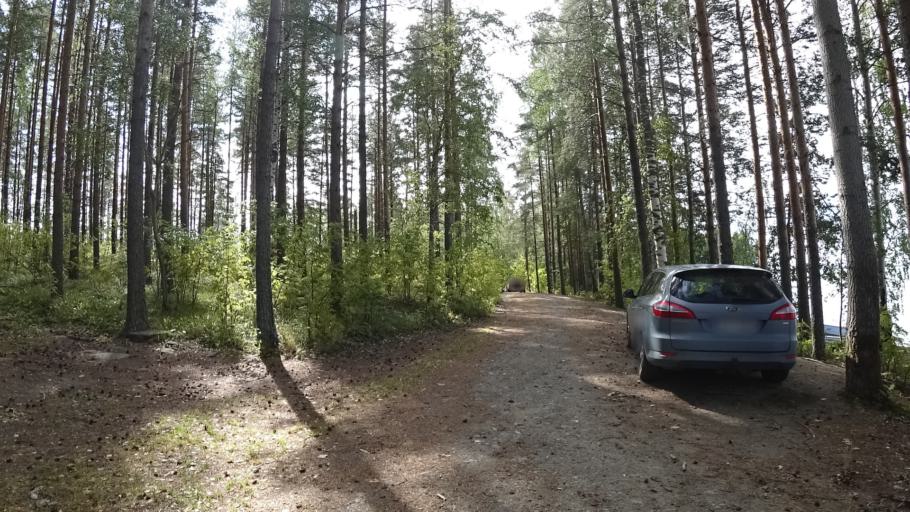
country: FI
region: North Karelia
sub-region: Keski-Karjala
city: Raeaekkylae
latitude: 62.3958
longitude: 29.7600
